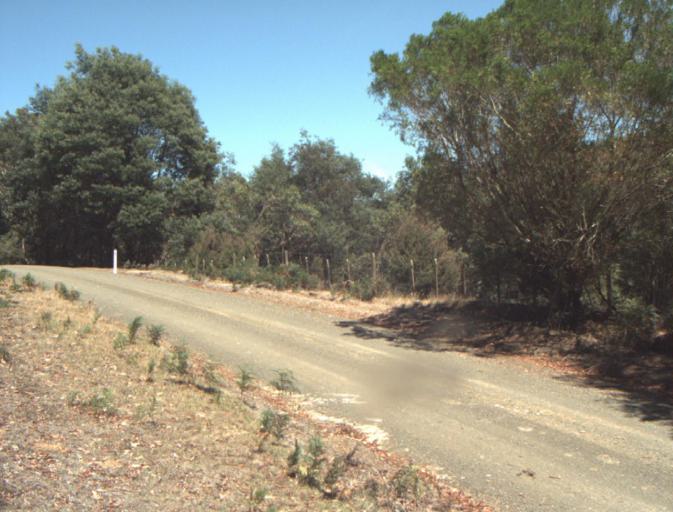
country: AU
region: Tasmania
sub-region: Dorset
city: Scottsdale
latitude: -41.2901
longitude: 147.3408
